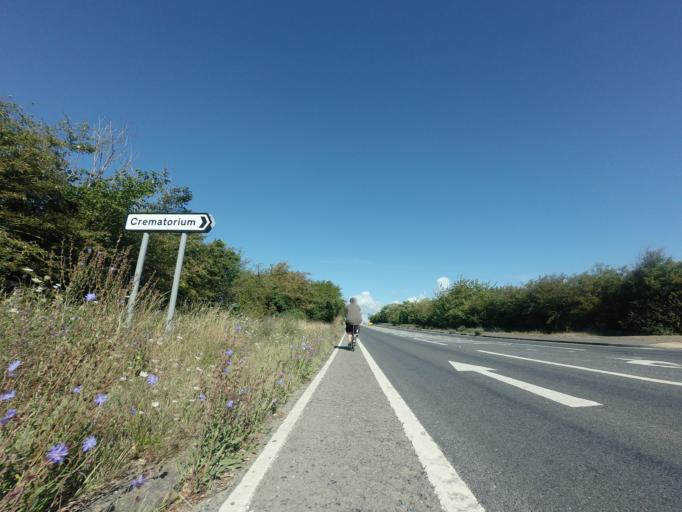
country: GB
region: England
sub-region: Kent
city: Gravesend
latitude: 51.4236
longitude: 0.4223
